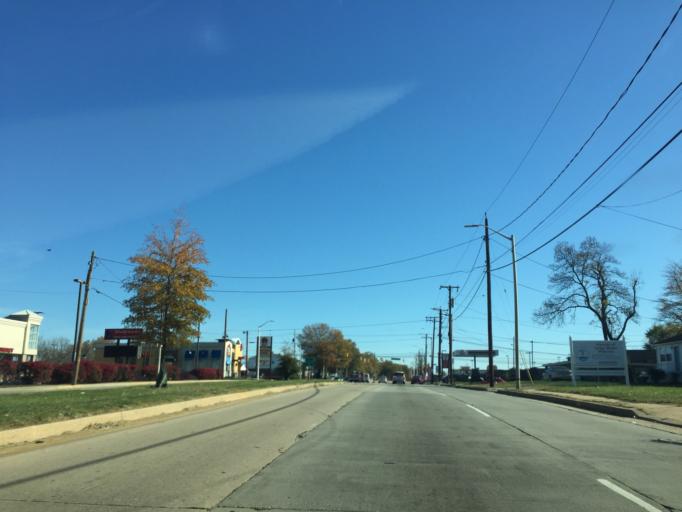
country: US
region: Maryland
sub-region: Baltimore County
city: Lansdowne
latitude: 39.2517
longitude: -76.6486
